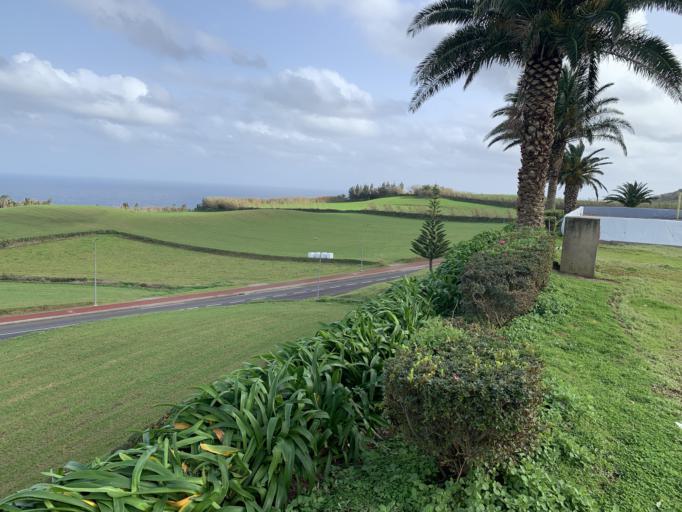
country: PT
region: Azores
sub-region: Povoacao
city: Furnas
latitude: 37.8315
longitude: -25.1449
